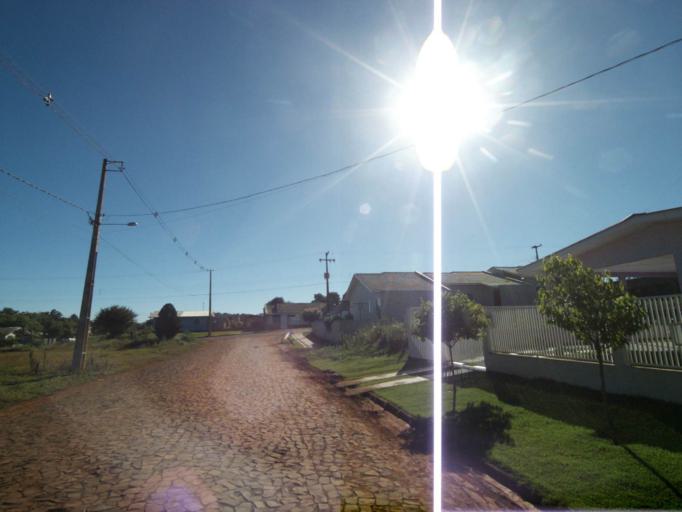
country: BR
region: Santa Catarina
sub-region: Sao Lourenco Do Oeste
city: Sao Lourenco dOeste
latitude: -26.2654
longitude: -52.7856
